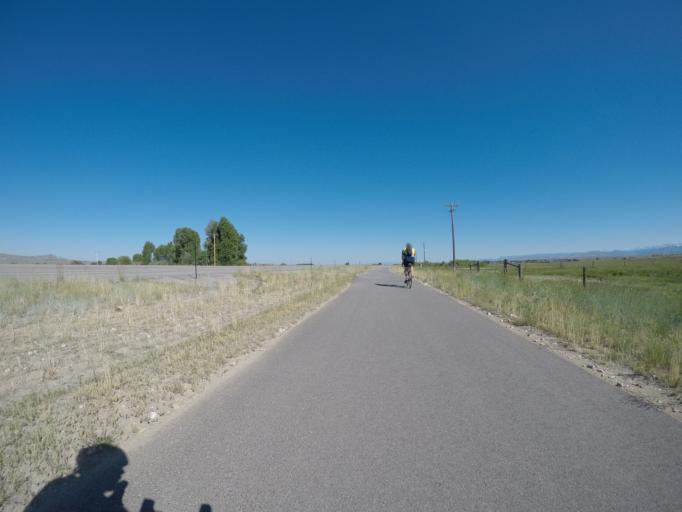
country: US
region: Wyoming
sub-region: Sublette County
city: Pinedale
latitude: 42.8225
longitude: -109.8421
